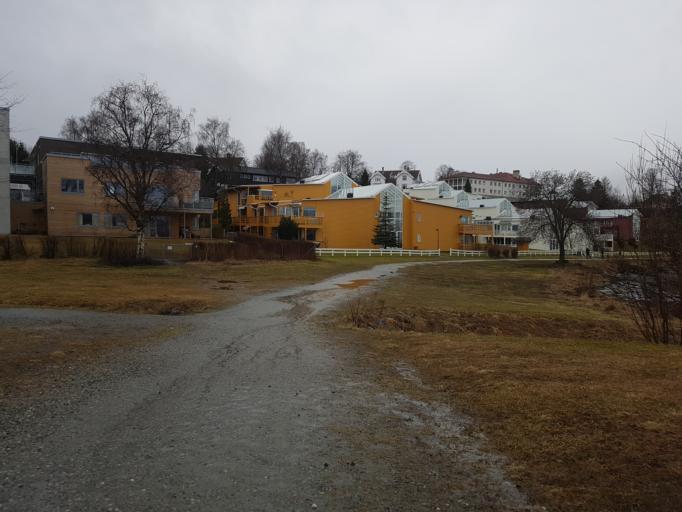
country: NO
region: Sor-Trondelag
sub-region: Trondheim
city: Trondheim
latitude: 63.4360
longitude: 10.4987
